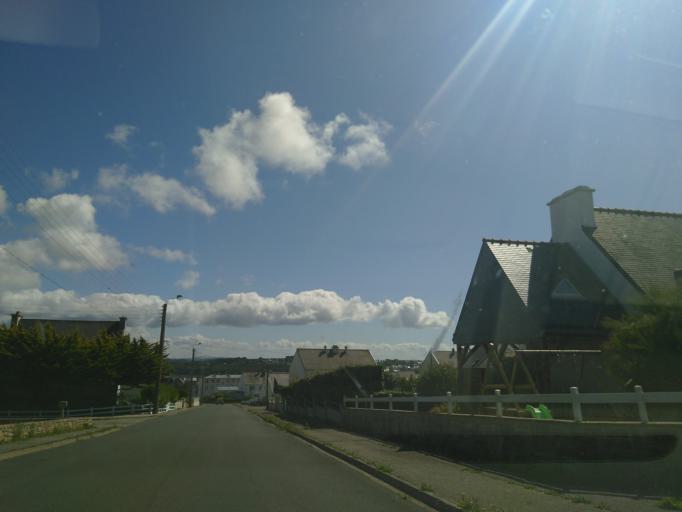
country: FR
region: Brittany
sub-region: Departement du Finistere
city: Camaret-sur-Mer
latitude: 48.2798
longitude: -4.6066
